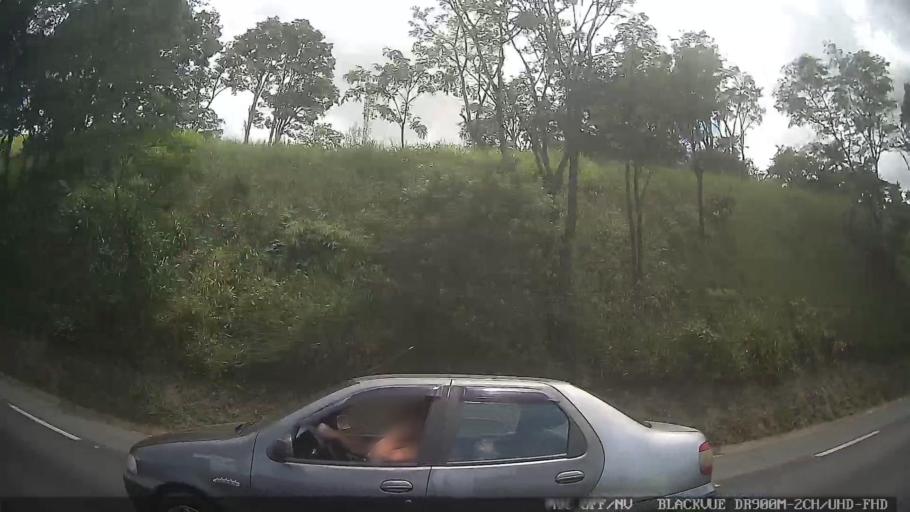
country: BR
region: Sao Paulo
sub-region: Atibaia
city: Atibaia
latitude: -23.1012
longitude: -46.6033
